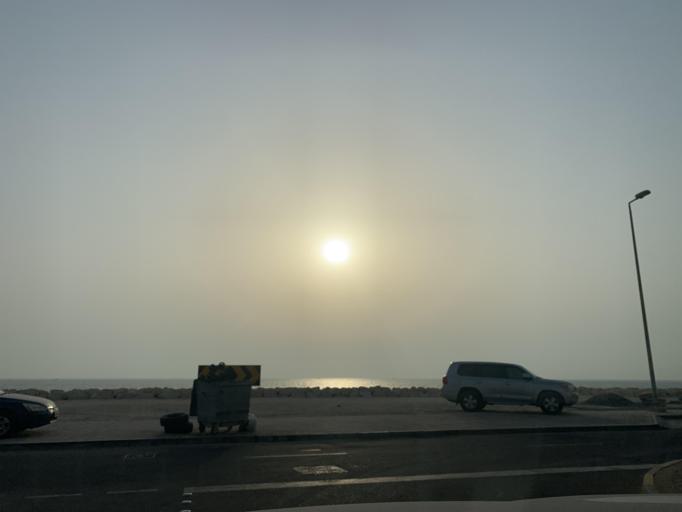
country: BH
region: Manama
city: Jidd Hafs
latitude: 26.2196
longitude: 50.4381
